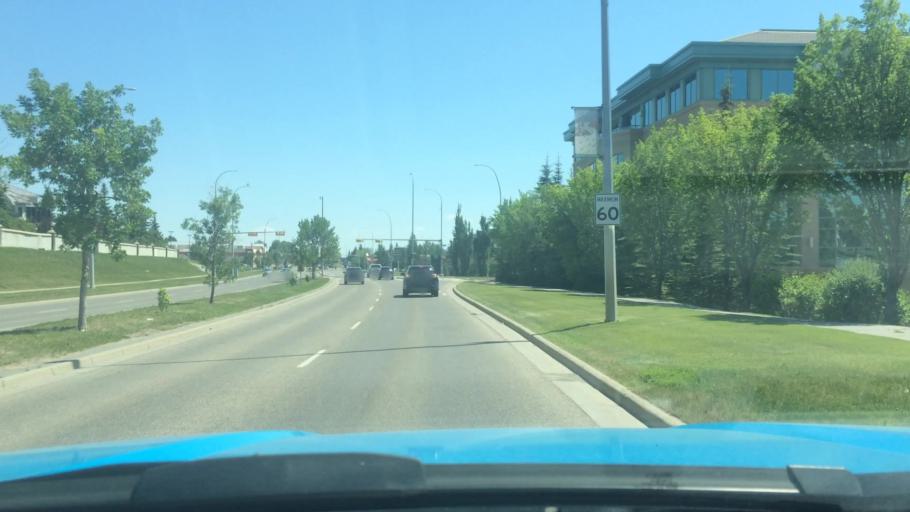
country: CA
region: Alberta
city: Calgary
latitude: 51.1306
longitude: -114.2013
